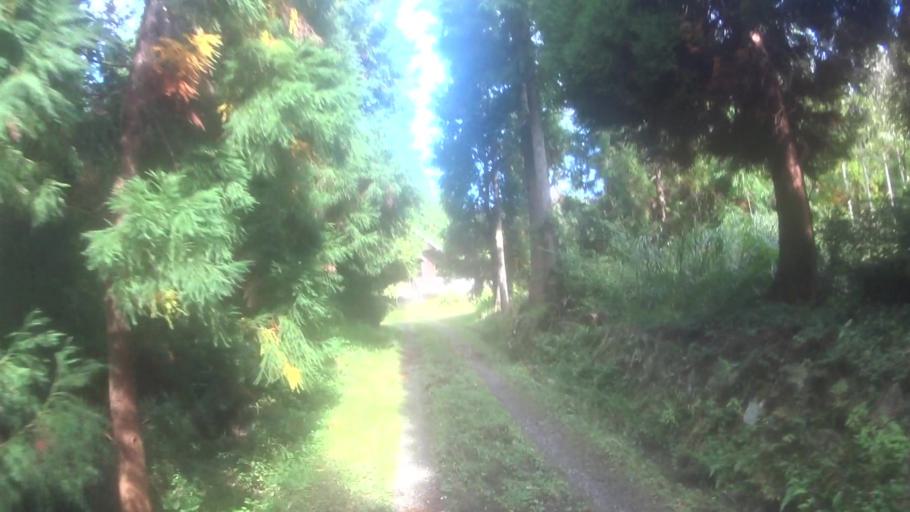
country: JP
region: Kyoto
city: Miyazu
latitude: 35.6247
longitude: 135.1631
